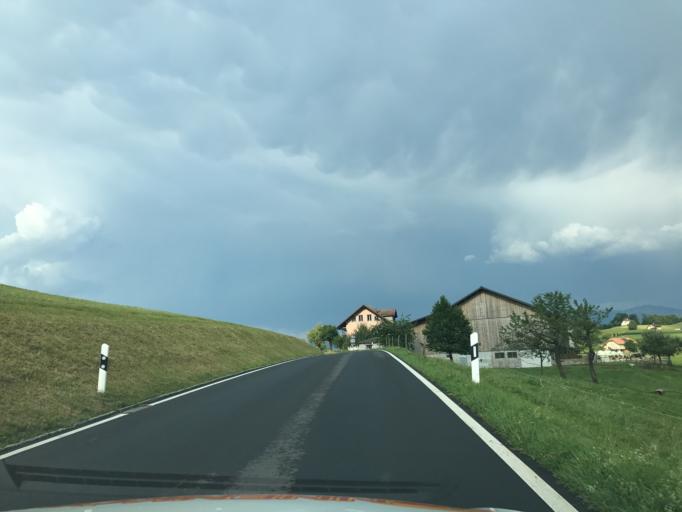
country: CH
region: Bern
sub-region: Thun District
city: Thierachern
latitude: 46.7200
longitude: 7.5570
